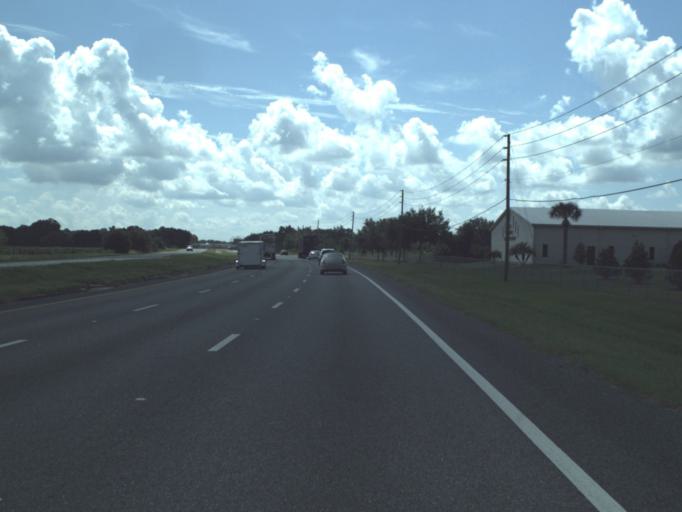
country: US
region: Florida
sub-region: Polk County
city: Lake Hamilton
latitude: 28.0771
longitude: -81.6485
